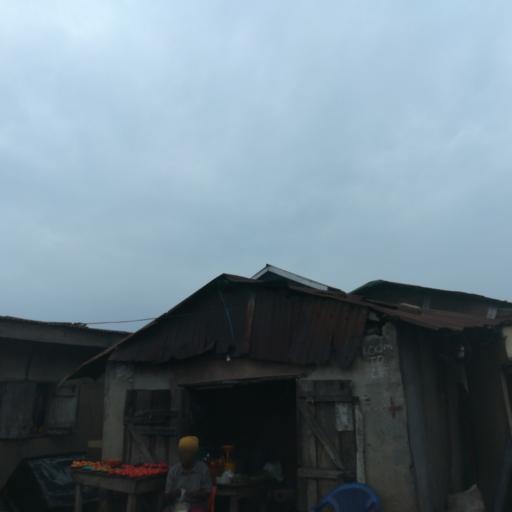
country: NG
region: Lagos
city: Makoko
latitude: 6.4979
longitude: 3.3895
